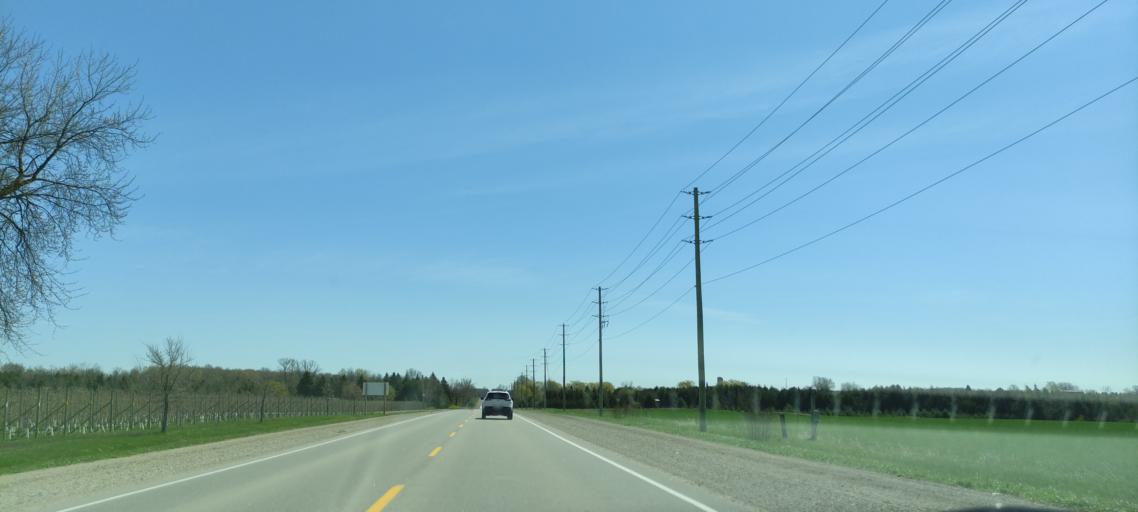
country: CA
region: Ontario
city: Waterloo
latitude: 43.5946
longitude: -80.5026
